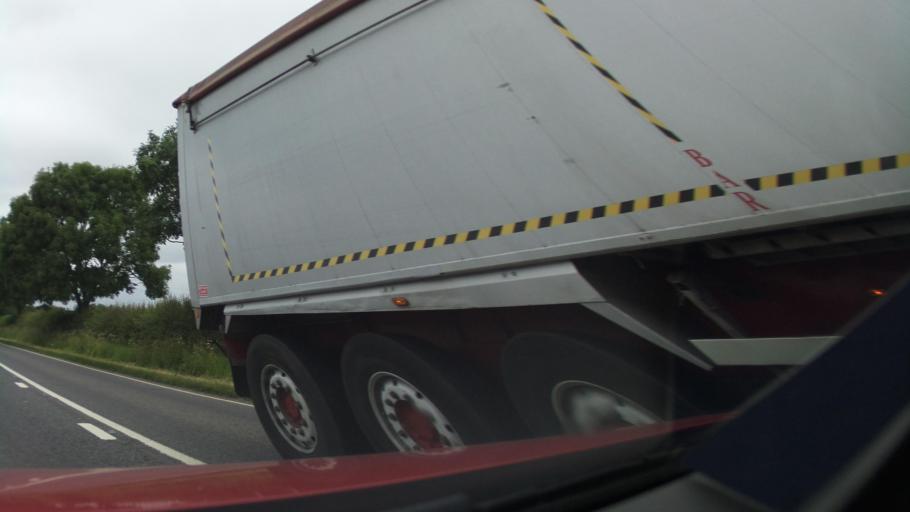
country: GB
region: England
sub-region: Nottinghamshire
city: East Leake
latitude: 52.8129
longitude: -1.1336
